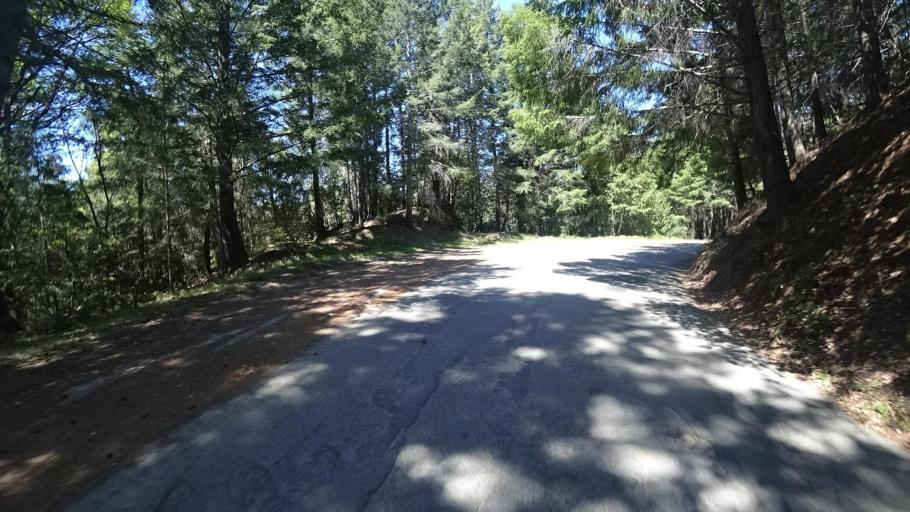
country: US
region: California
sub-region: Humboldt County
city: Redway
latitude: 40.1076
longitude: -123.9560
